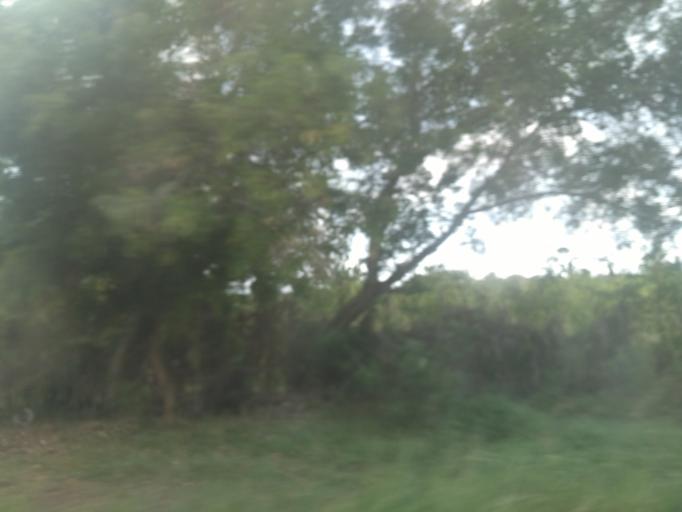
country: TZ
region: Zanzibar Urban/West
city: Zanzibar
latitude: -6.2813
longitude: 39.2790
